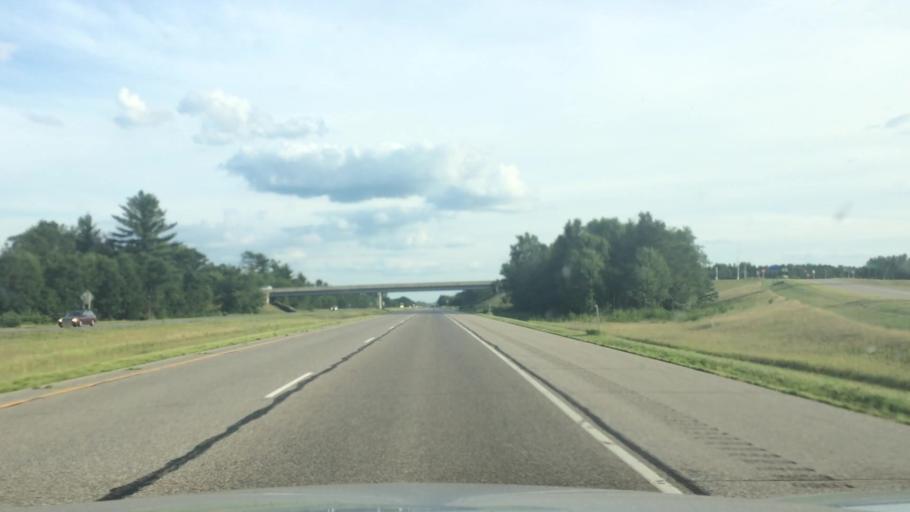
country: US
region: Wisconsin
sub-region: Portage County
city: Plover
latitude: 44.3117
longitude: -89.5236
